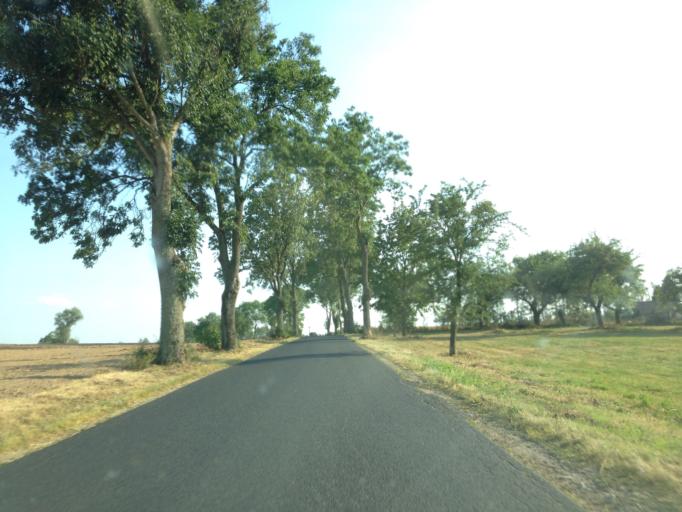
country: PL
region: Kujawsko-Pomorskie
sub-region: Powiat brodnicki
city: Brodnica
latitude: 53.3750
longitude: 19.3735
